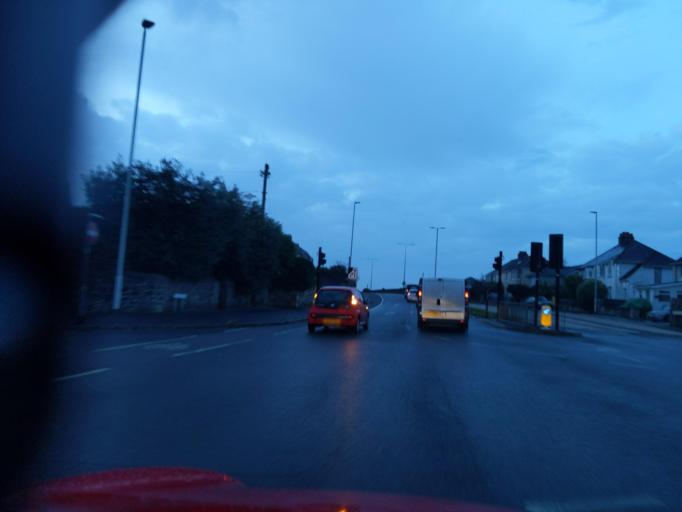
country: GB
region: England
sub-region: Plymouth
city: Plymstock
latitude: 50.3614
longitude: -4.0660
